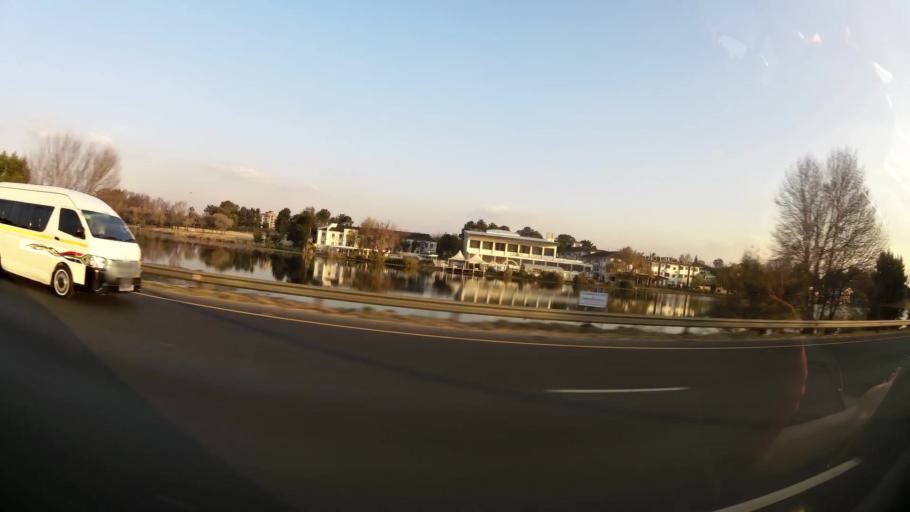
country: ZA
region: Gauteng
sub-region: Ekurhuleni Metropolitan Municipality
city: Benoni
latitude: -26.1807
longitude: 28.3043
